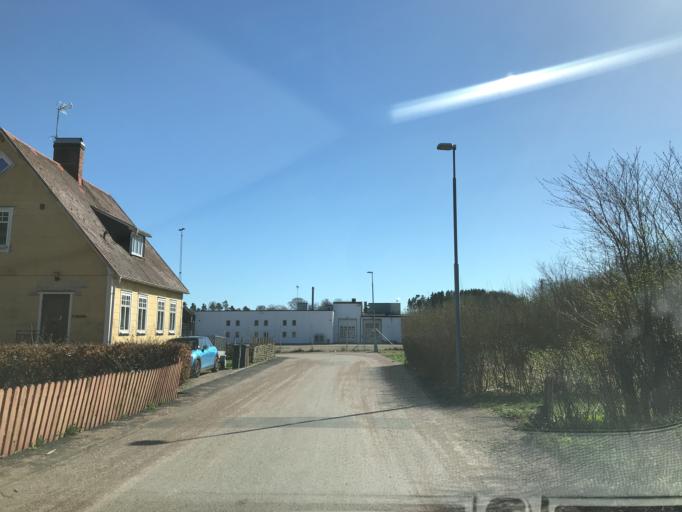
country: SE
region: Skane
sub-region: Svalovs Kommun
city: Kagerod
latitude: 55.9982
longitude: 13.0839
